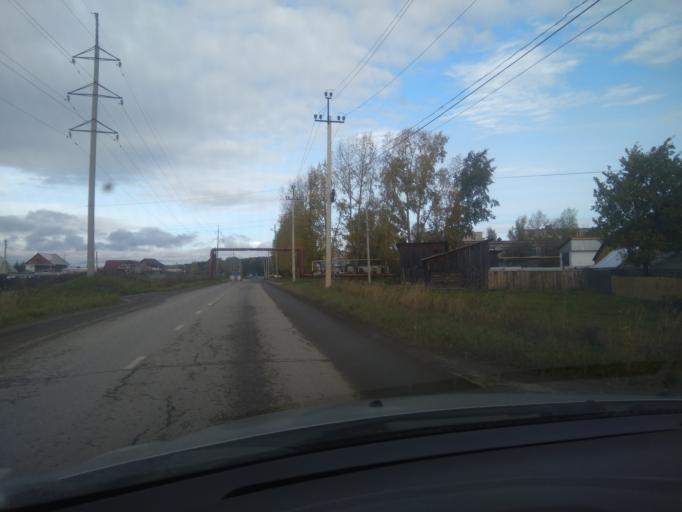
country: RU
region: Sverdlovsk
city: Nikolo-Pavlovskoye
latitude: 57.7968
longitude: 60.0516
